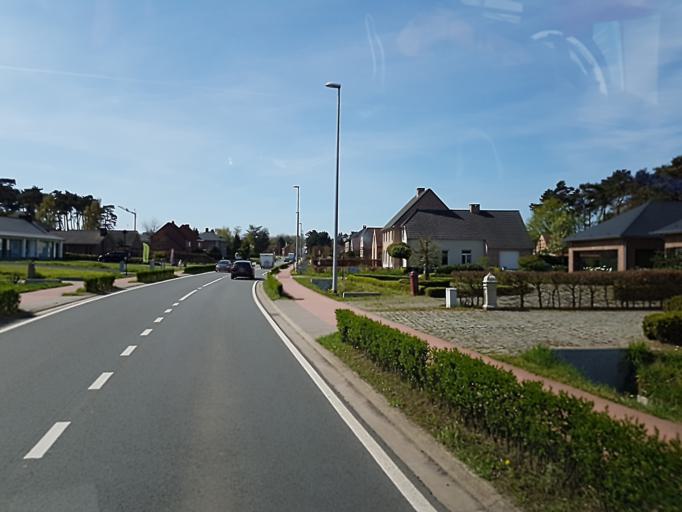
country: BE
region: Flanders
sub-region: Provincie Antwerpen
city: Herselt
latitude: 51.0624
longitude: 4.8902
